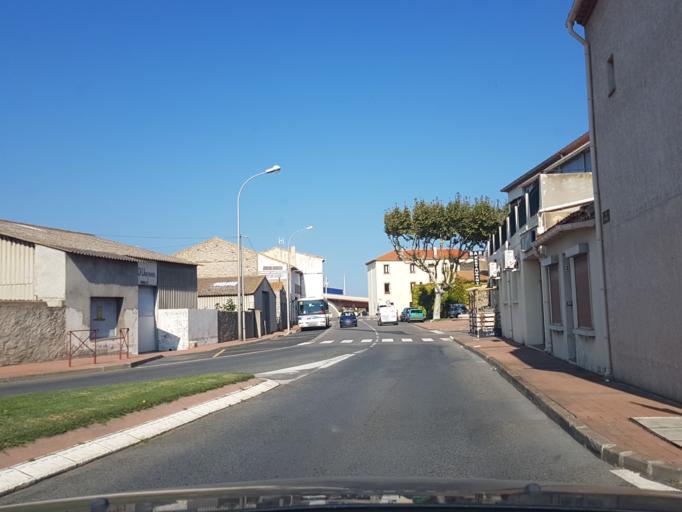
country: FR
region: Languedoc-Roussillon
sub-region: Departement de l'Aude
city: Port-la-Nouvelle
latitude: 43.0227
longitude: 3.0395
